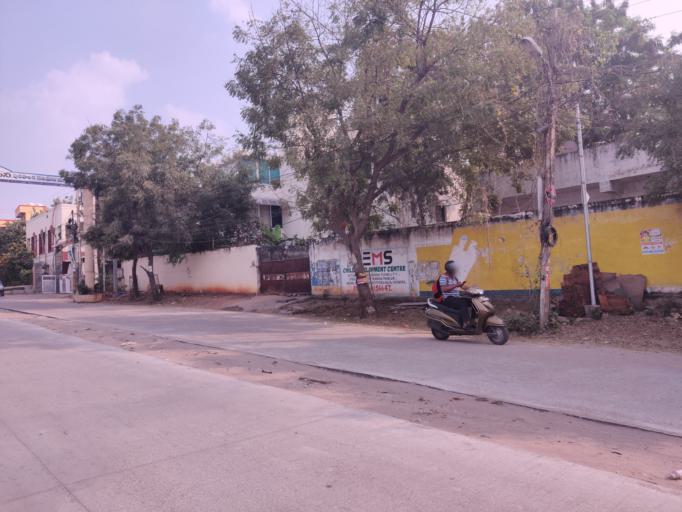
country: IN
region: Telangana
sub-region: Hyderabad
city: Hyderabad
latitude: 17.4033
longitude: 78.3902
